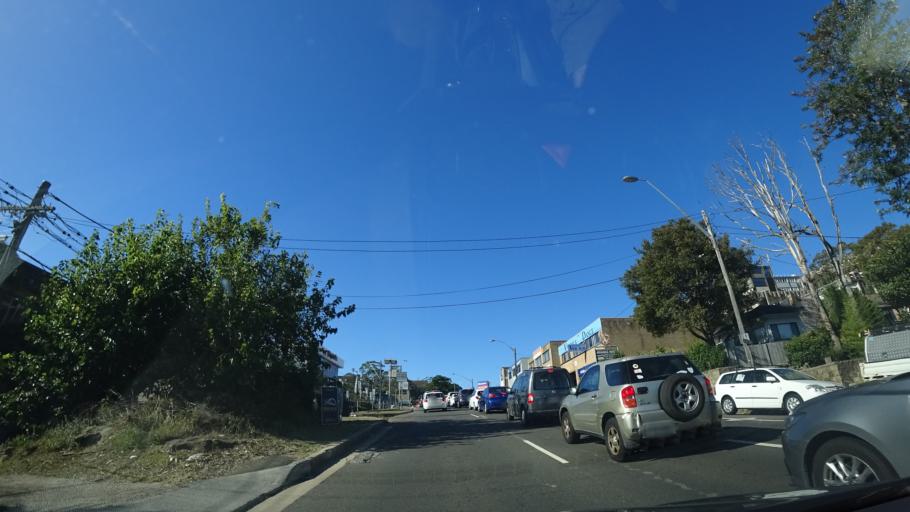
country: AU
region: New South Wales
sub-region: Warringah
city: Brookvale
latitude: -33.7601
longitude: 151.2805
